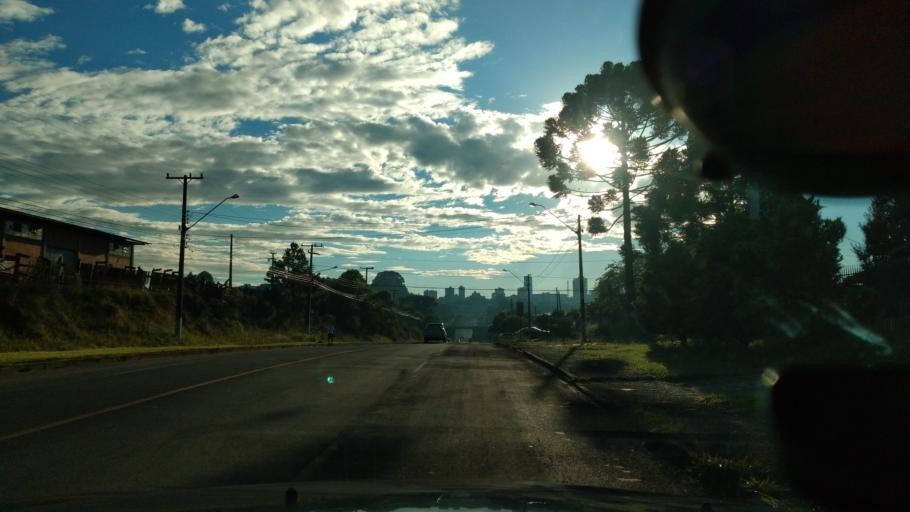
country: BR
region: Parana
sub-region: Guarapuava
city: Guarapuava
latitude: -25.3937
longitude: -51.4891
